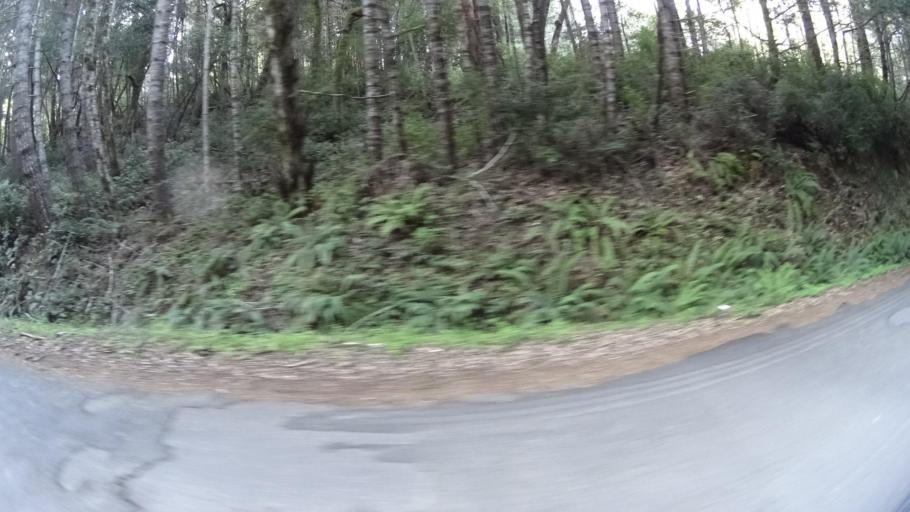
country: US
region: California
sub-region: Humboldt County
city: Blue Lake
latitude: 40.7020
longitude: -123.9398
